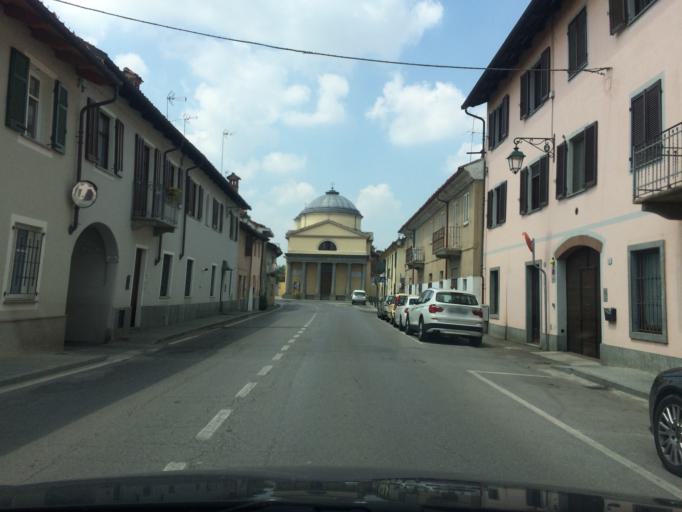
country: IT
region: Piedmont
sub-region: Provincia di Cuneo
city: Racconigi
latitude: 44.7666
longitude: 7.6736
